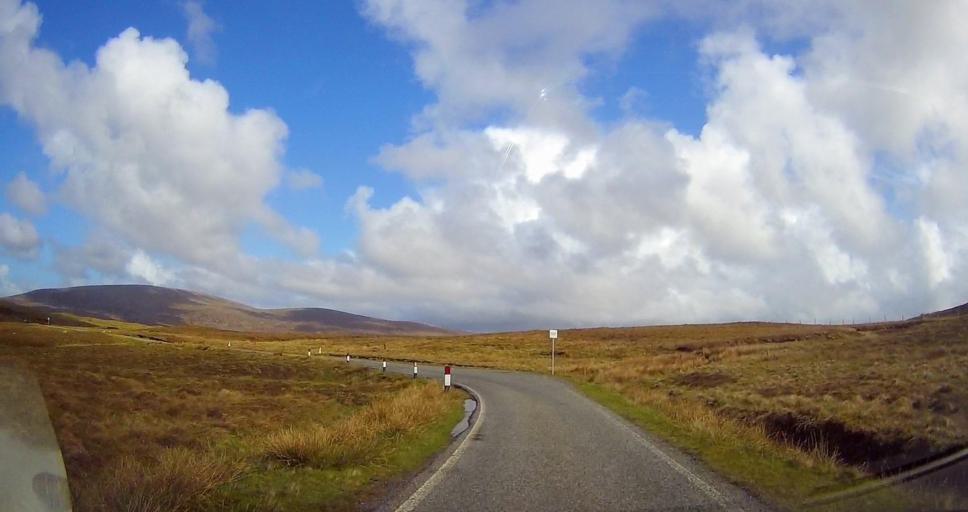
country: GB
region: Scotland
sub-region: Shetland Islands
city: Lerwick
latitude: 60.4949
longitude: -1.3916
